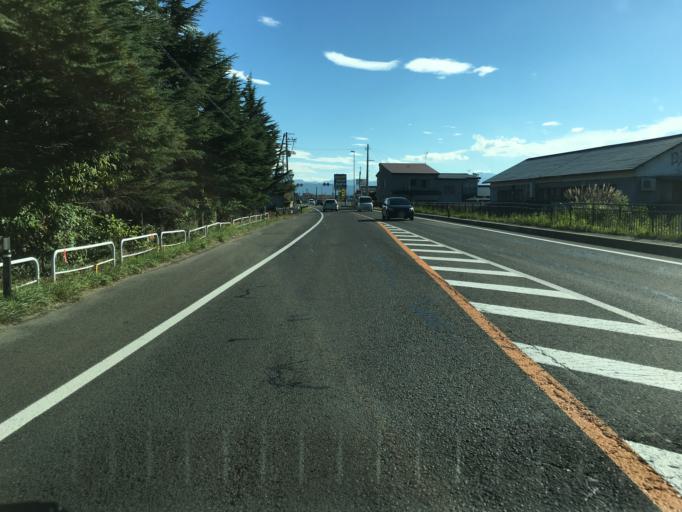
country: JP
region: Yamagata
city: Takahata
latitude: 37.9849
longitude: 140.1395
